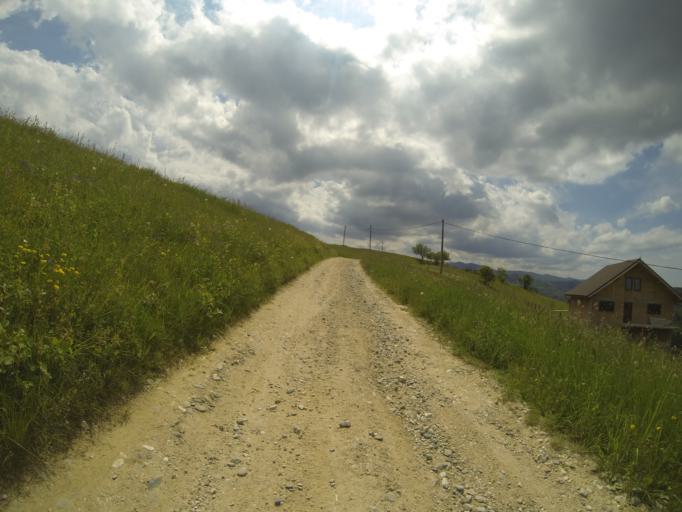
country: RO
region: Brasov
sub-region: Comuna Poiana Marului
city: Poiana Marului
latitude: 45.6242
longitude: 25.3181
